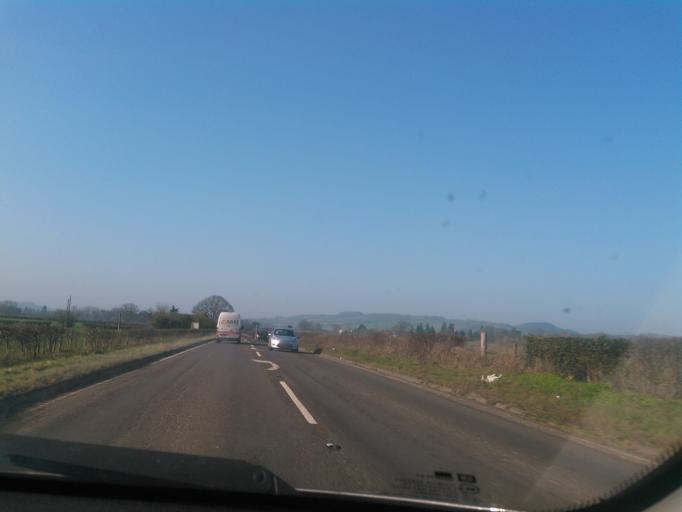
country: GB
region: England
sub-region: Shropshire
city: Craven Arms
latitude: 52.4677
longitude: -2.8228
